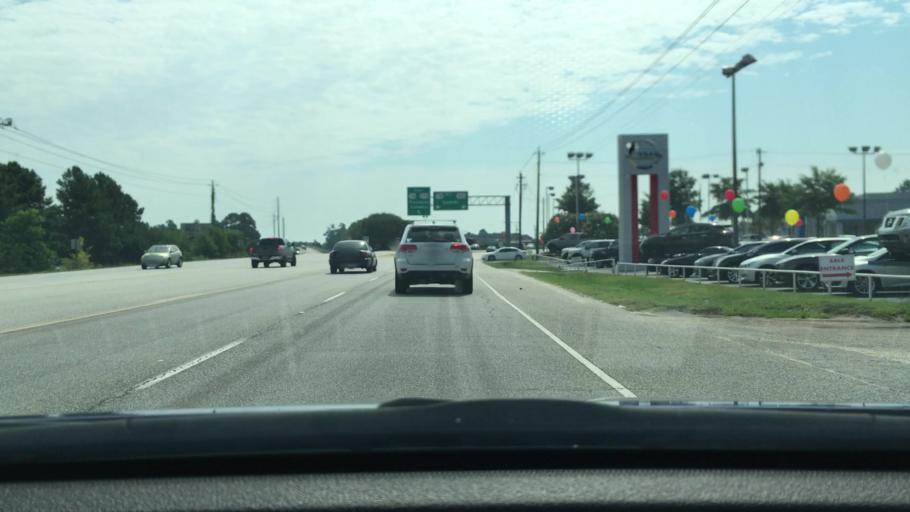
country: US
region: South Carolina
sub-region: Sumter County
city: Sumter
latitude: 33.9566
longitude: -80.3861
